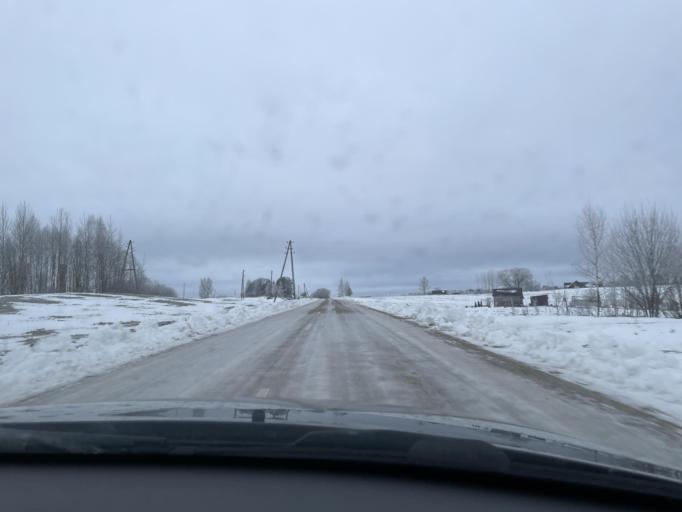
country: LV
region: Ludzas Rajons
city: Ludza
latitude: 56.4382
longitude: 27.5408
